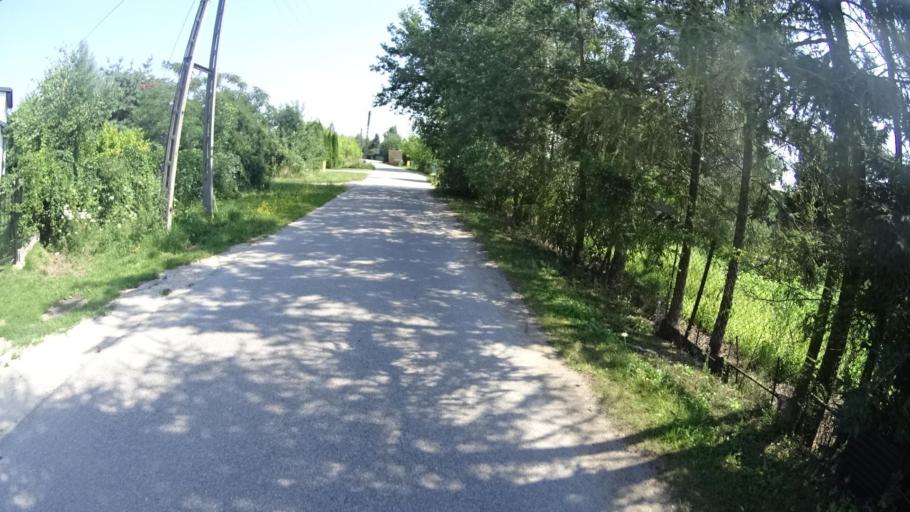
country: PL
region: Masovian Voivodeship
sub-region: Powiat grojecki
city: Grojec
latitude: 51.8519
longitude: 20.8619
